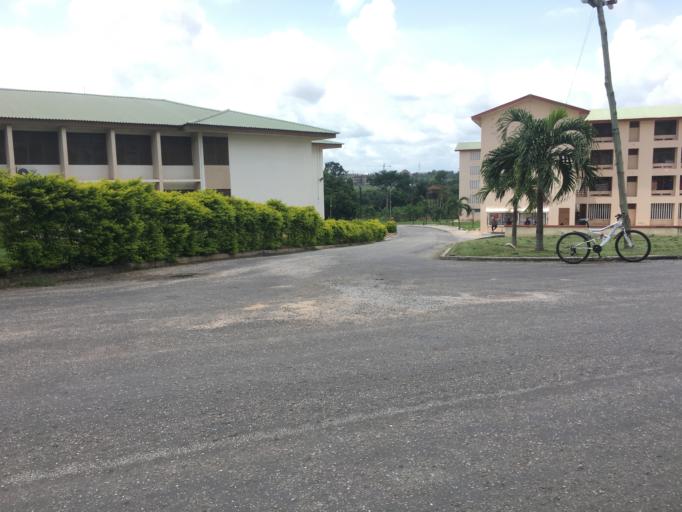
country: GH
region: Ashanti
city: Kumasi
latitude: 6.6713
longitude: -1.5736
